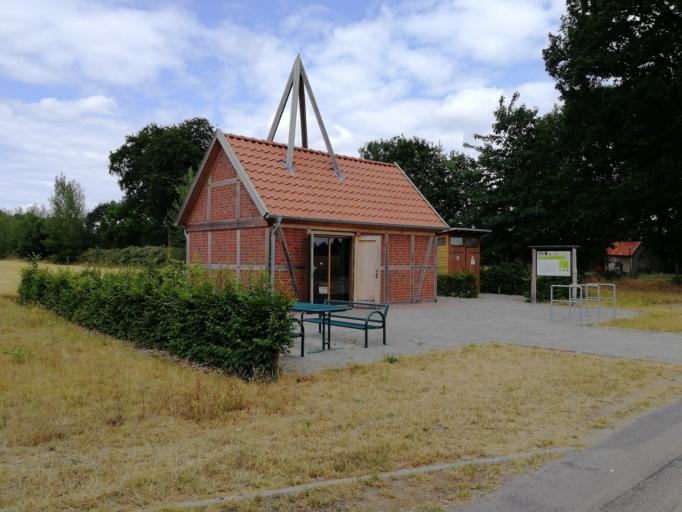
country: DE
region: Lower Saxony
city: Salzbergen
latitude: 52.3231
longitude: 7.3706
